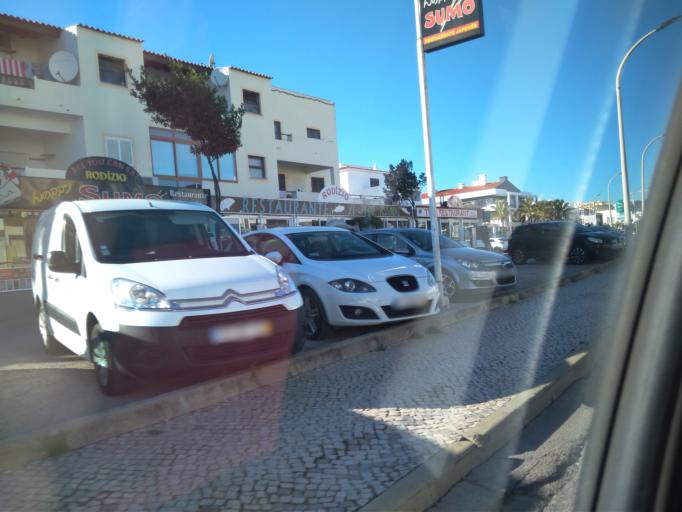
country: PT
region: Faro
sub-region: Albufeira
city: Albufeira
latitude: 37.0912
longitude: -8.2221
